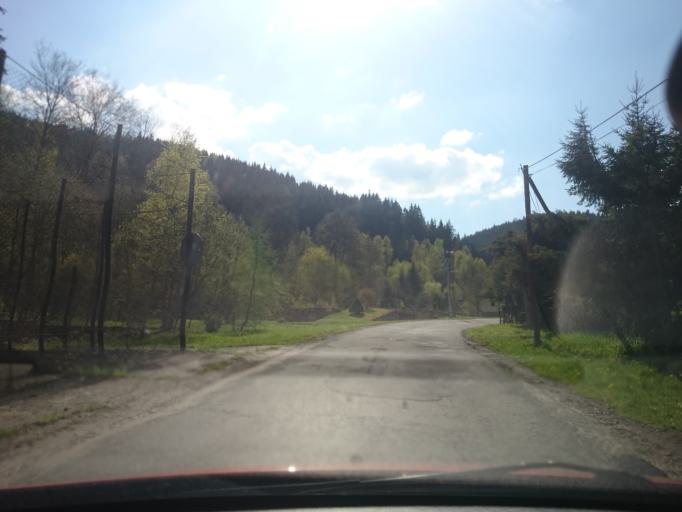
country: PL
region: Lower Silesian Voivodeship
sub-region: Powiat klodzki
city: Polanica-Zdroj
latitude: 50.3036
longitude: 16.5305
